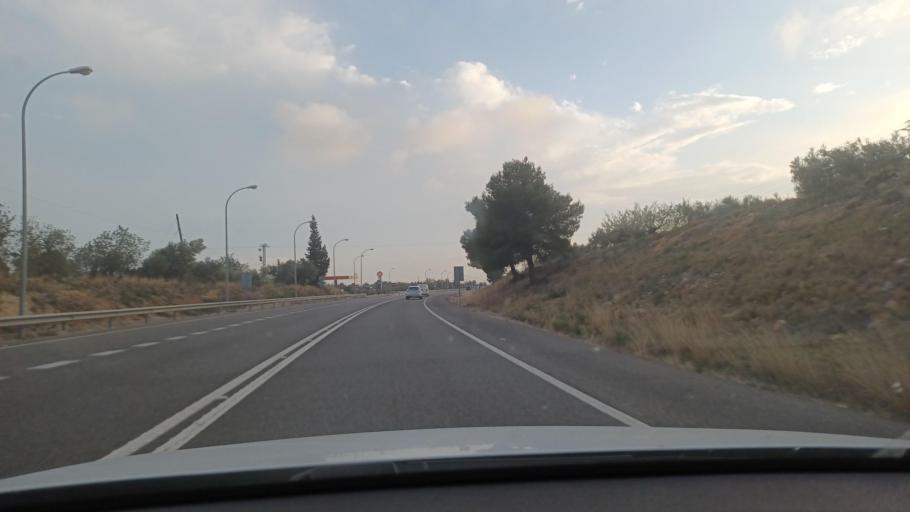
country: ES
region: Catalonia
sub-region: Provincia de Tarragona
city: L'Ampolla
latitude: 40.8394
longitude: 0.7113
